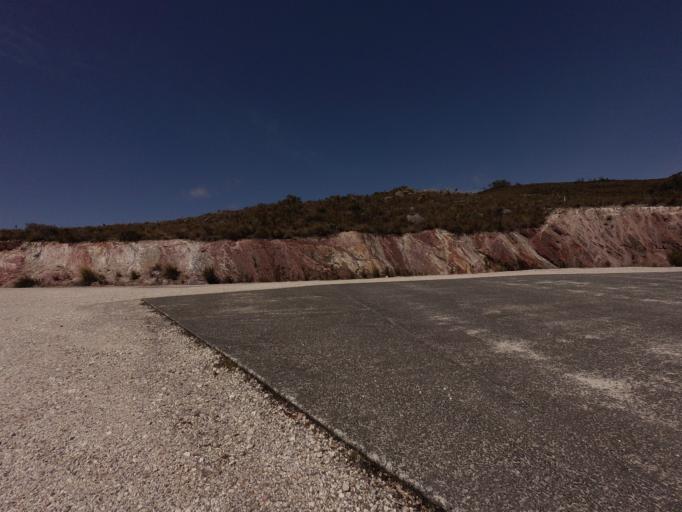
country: AU
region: Tasmania
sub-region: Huon Valley
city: Geeveston
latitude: -43.0308
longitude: 146.2913
